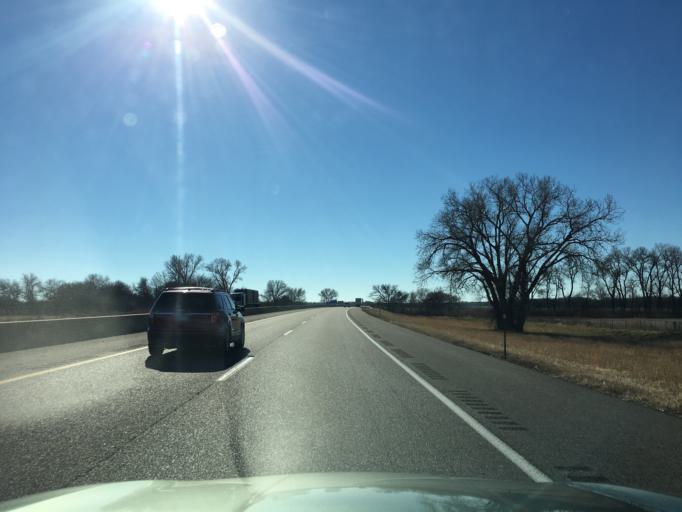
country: US
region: Kansas
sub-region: Sumner County
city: Belle Plaine
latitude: 37.4164
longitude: -97.3213
